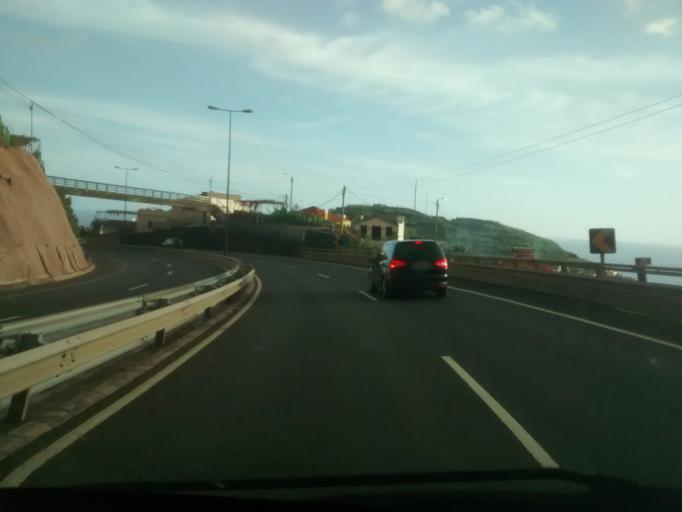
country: PT
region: Madeira
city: Camara de Lobos
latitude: 32.6589
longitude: -16.9762
